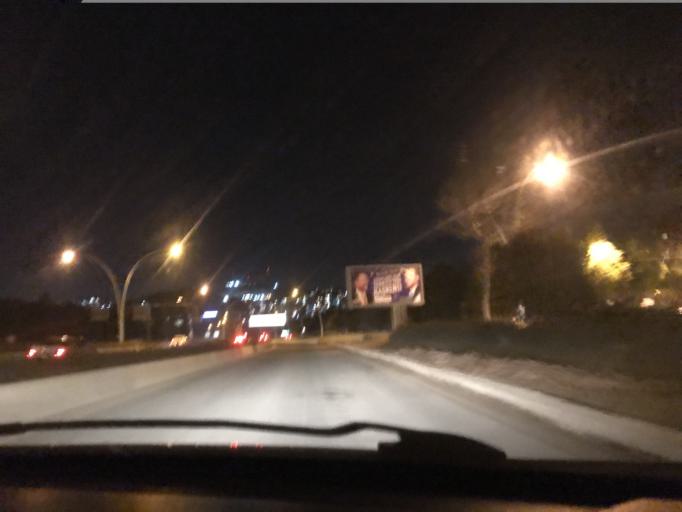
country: TR
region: Ankara
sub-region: Goelbasi
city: Golbasi
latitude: 39.8431
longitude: 32.8068
